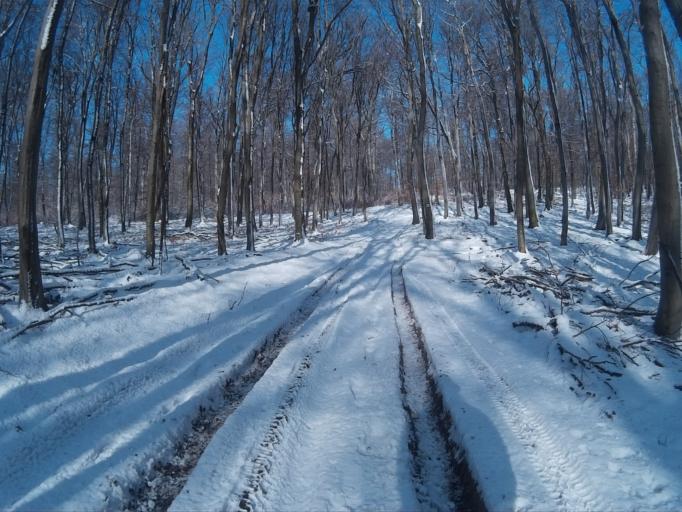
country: HU
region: Komarom-Esztergom
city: Labatlan
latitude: 47.7049
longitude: 18.5119
